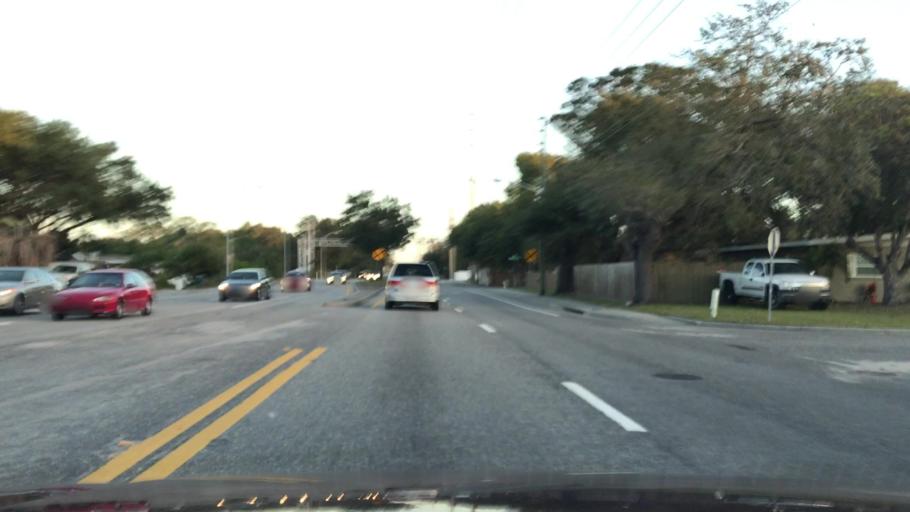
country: US
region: Florida
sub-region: Sarasota County
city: Sarasota
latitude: 27.3289
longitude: -82.5140
